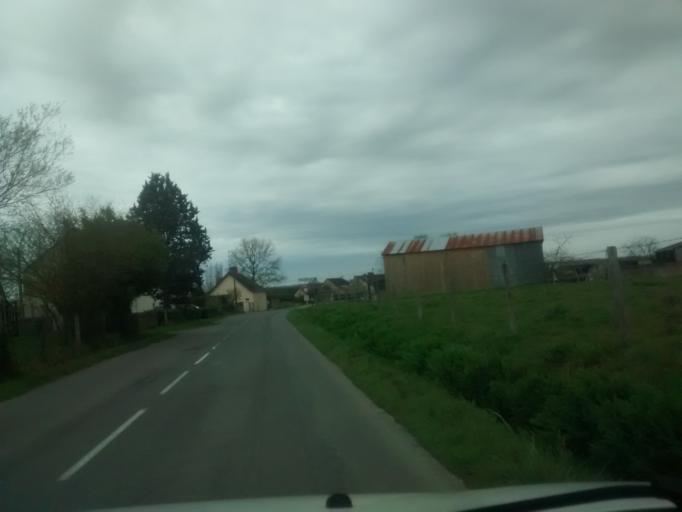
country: FR
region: Brittany
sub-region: Departement d'Ille-et-Vilaine
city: Betton
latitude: 48.1792
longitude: -1.6193
